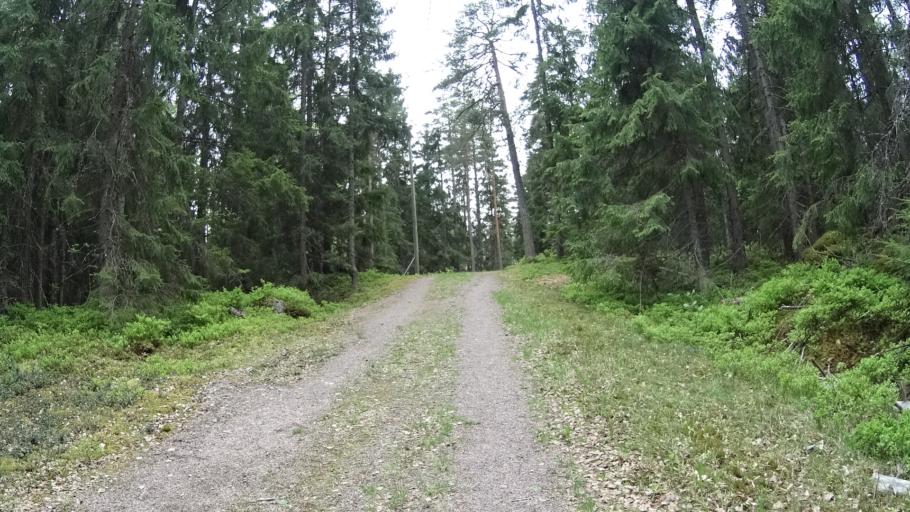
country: FI
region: Uusimaa
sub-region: Helsinki
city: Espoo
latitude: 60.2381
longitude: 24.6754
